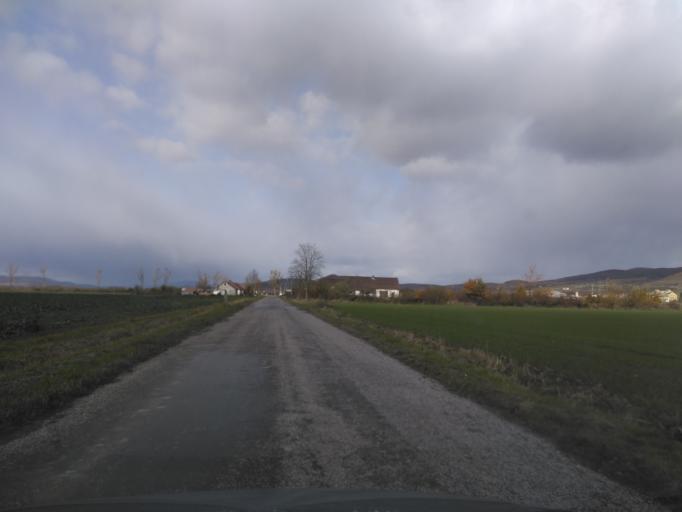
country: HU
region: Borsod-Abauj-Zemplen
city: Satoraljaujhely
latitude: 48.4201
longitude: 21.6774
